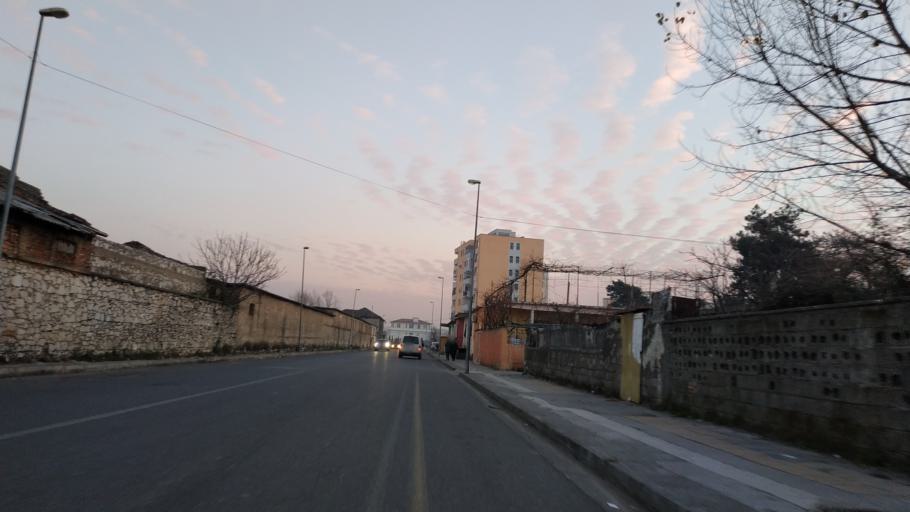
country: AL
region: Shkoder
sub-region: Rrethi i Shkodres
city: Shkoder
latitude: 42.0771
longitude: 19.5234
